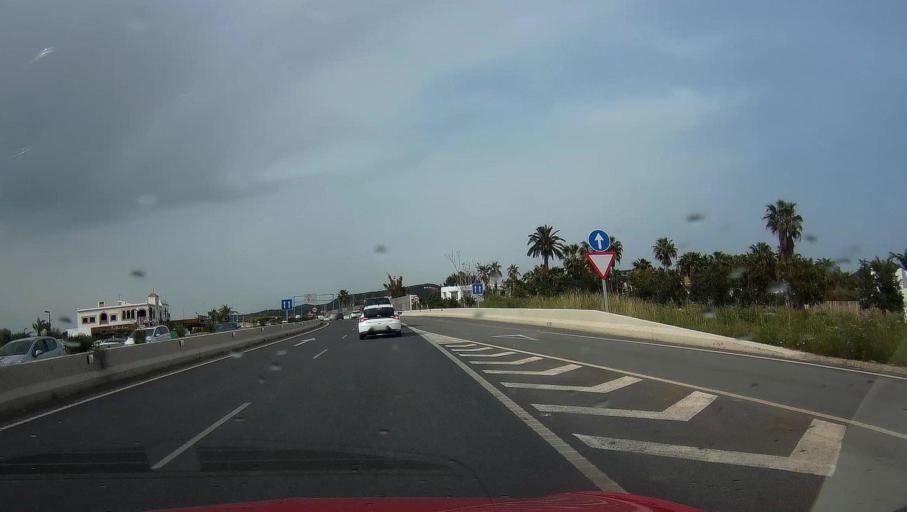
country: ES
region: Balearic Islands
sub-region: Illes Balears
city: Ibiza
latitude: 38.9328
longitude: 1.4440
